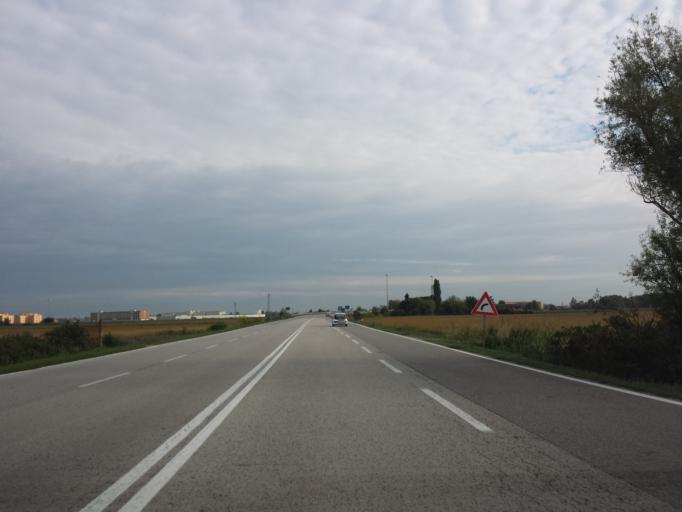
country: IT
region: Veneto
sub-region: Provincia di Rovigo
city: Rovigo
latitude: 45.0901
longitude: 11.8028
